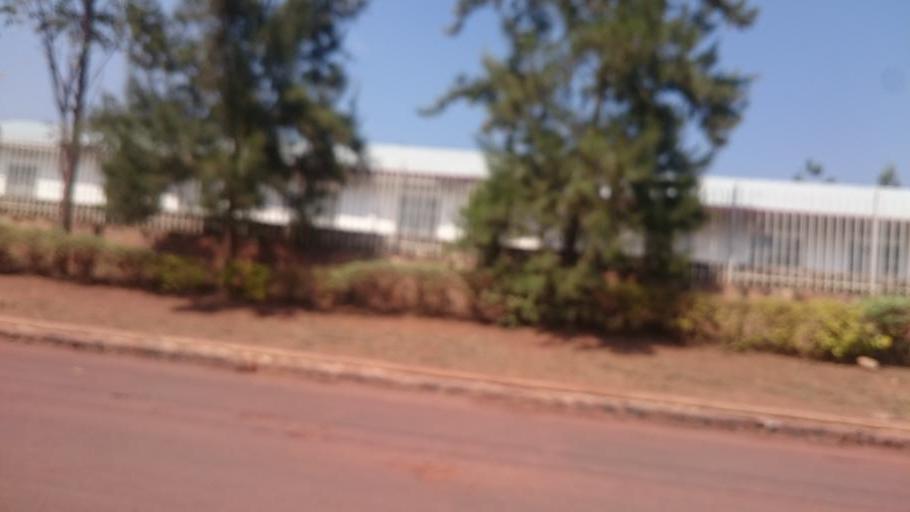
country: RW
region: Kigali
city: Kigali
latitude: -1.9415
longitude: 30.0888
